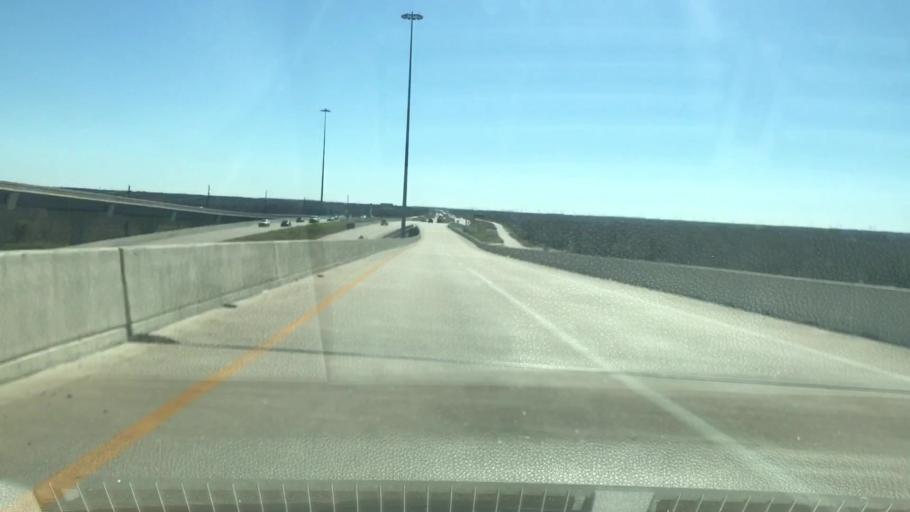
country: US
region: Texas
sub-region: Harris County
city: Cypress
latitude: 29.9953
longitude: -95.7691
